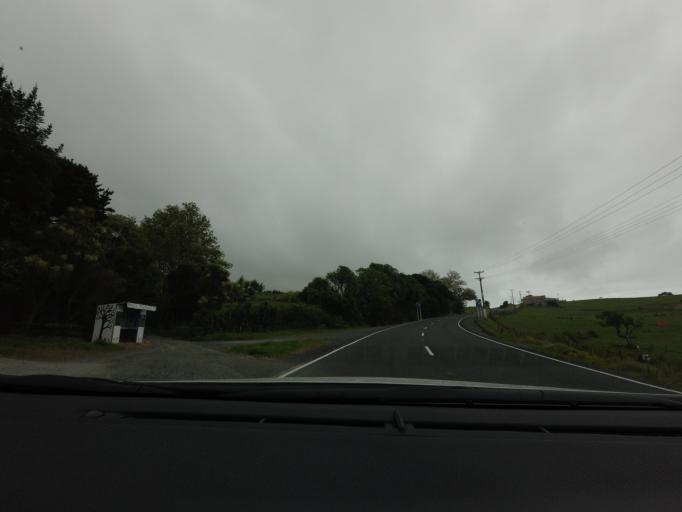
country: NZ
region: Auckland
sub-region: Auckland
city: Warkworth
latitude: -36.2884
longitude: 174.7973
